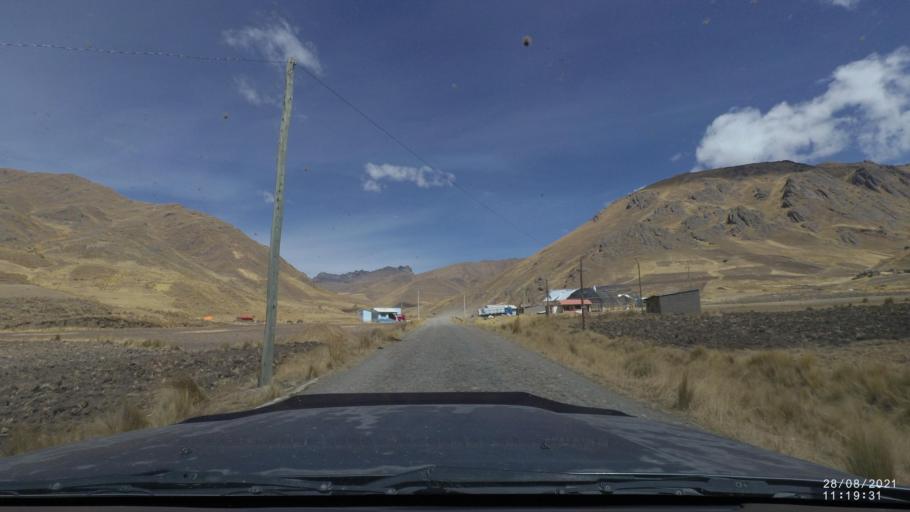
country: BO
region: Cochabamba
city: Cochabamba
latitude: -17.1541
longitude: -66.3333
